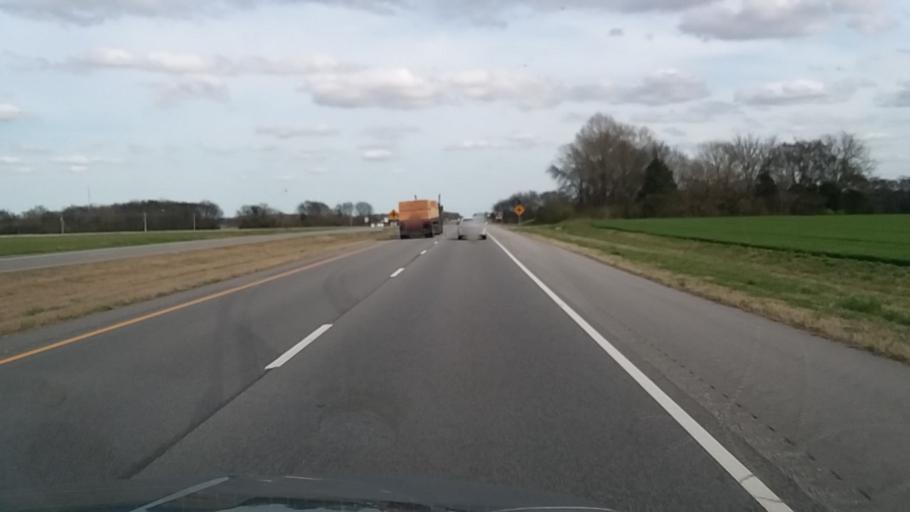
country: US
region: Alabama
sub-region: Lawrence County
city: Town Creek
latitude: 34.6839
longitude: -87.5339
